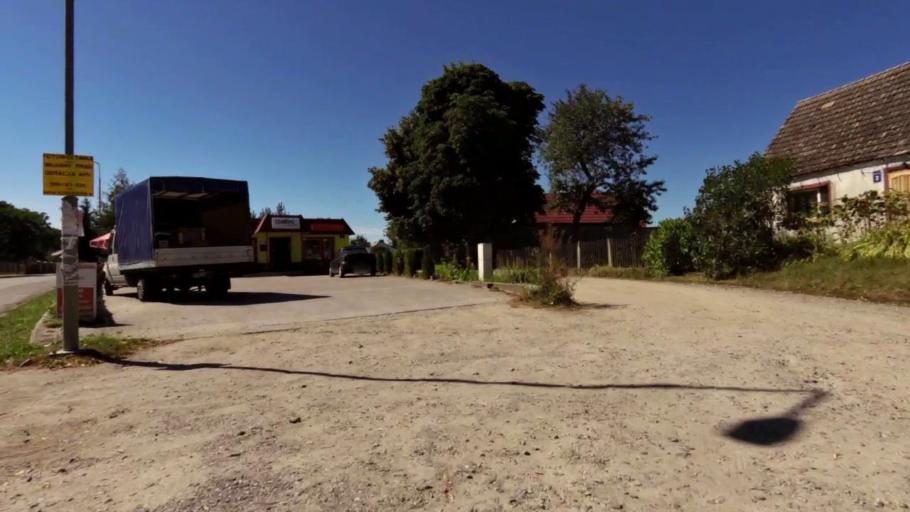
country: PL
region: West Pomeranian Voivodeship
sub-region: Powiat szczecinecki
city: Szczecinek
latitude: 53.7177
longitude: 16.6364
